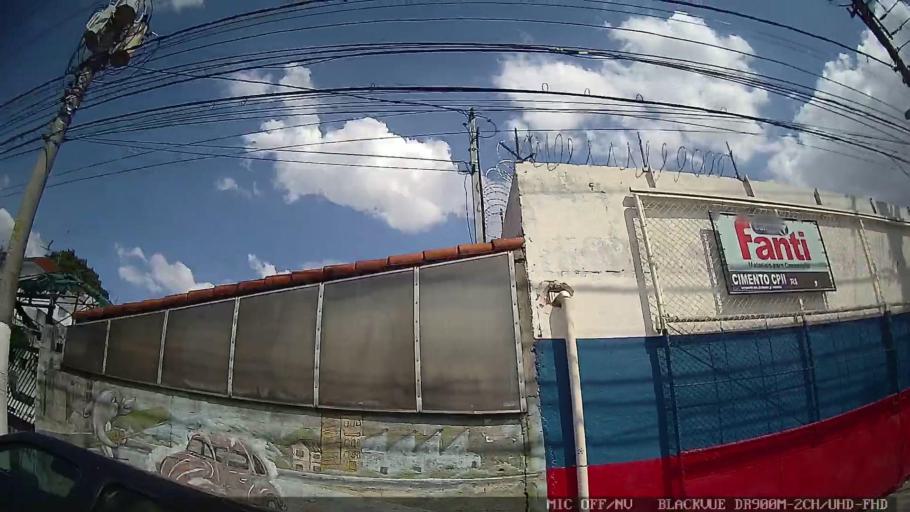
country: BR
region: Sao Paulo
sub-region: Guarulhos
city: Guarulhos
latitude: -23.5151
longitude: -46.5074
